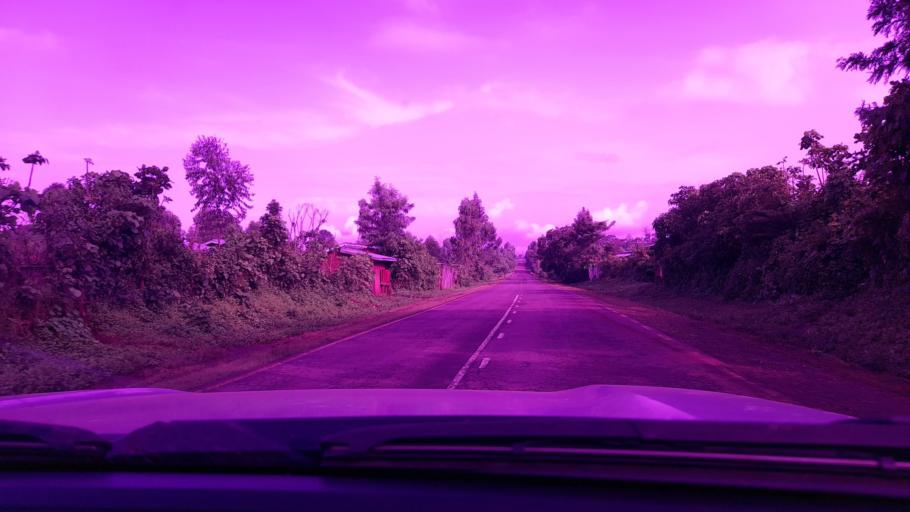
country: ET
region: Oromiya
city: Bedele
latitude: 8.1832
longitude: 36.4529
